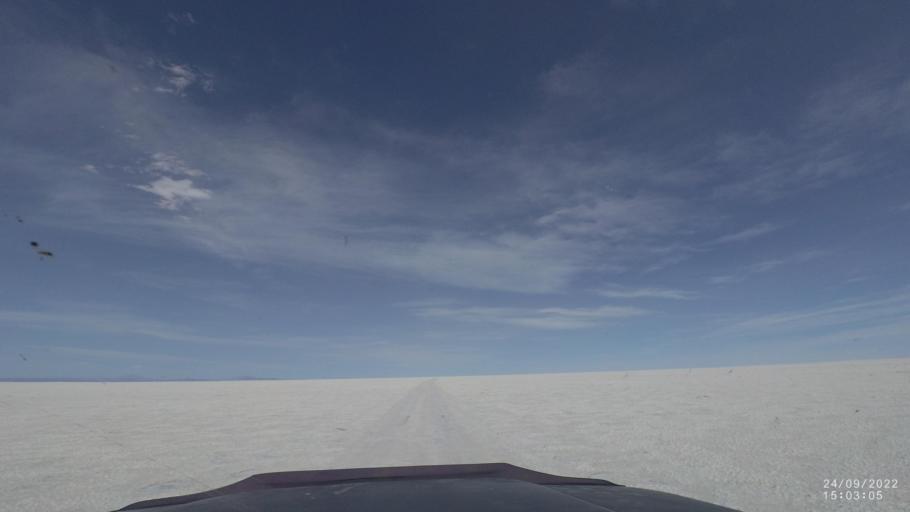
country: BO
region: Potosi
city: Colchani
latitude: -19.8926
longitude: -67.5324
